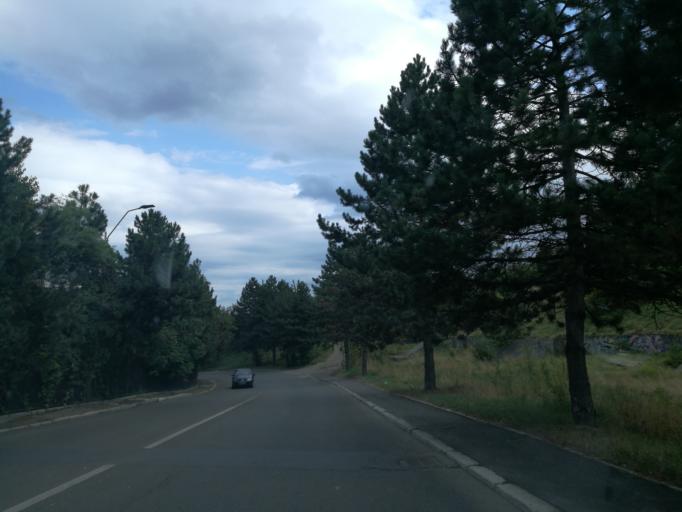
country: RO
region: Suceava
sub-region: Comuna Scheia
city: Scheia
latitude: 47.6555
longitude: 26.2521
